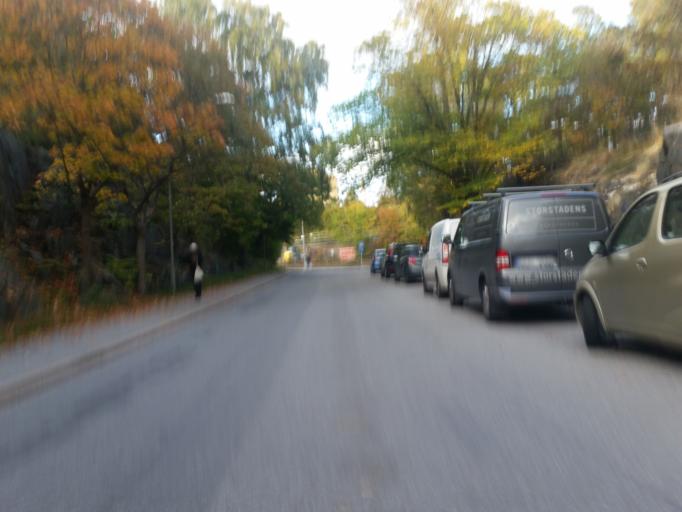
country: SE
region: Stockholm
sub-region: Stockholms Kommun
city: Arsta
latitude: 59.2958
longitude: 18.0860
